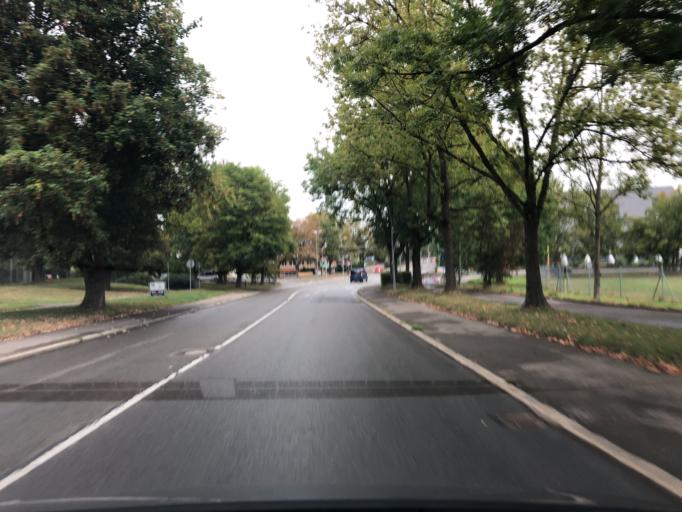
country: DE
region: Baden-Wuerttemberg
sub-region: Regierungsbezirk Stuttgart
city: Sindelfingen
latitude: 48.7210
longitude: 9.0081
